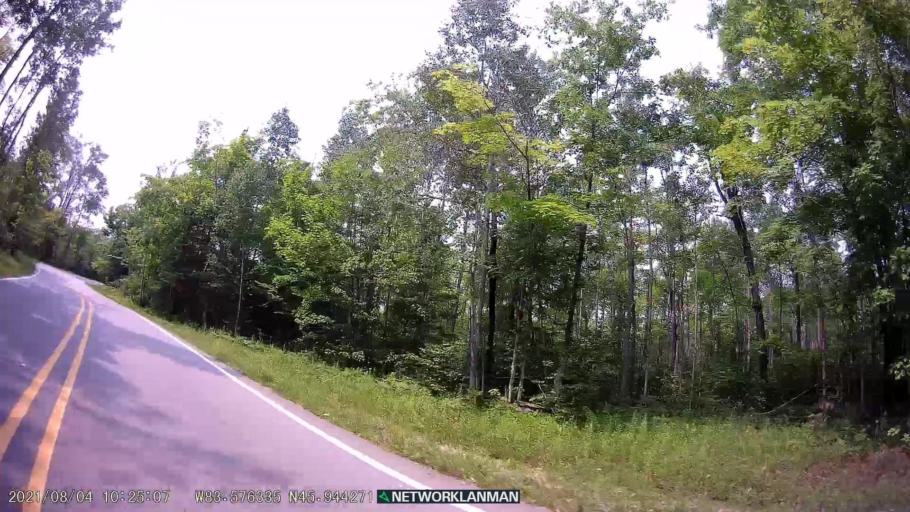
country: CA
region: Ontario
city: Thessalon
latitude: 45.9442
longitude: -83.5764
